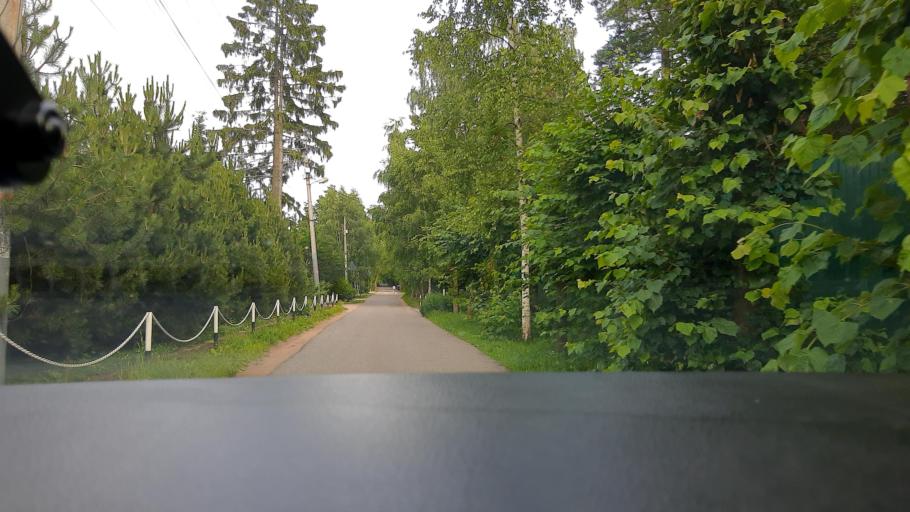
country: RU
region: Moscow
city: Novo-Peredelkino
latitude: 55.6772
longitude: 37.3316
